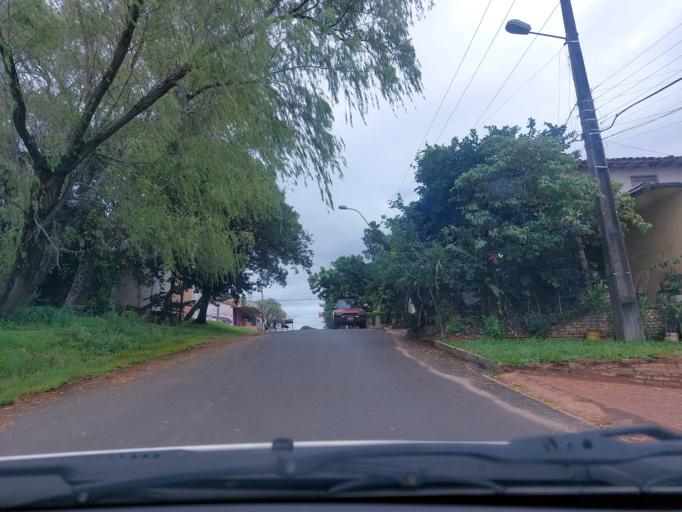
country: PY
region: San Pedro
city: Guayaybi
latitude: -24.6622
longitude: -56.4394
